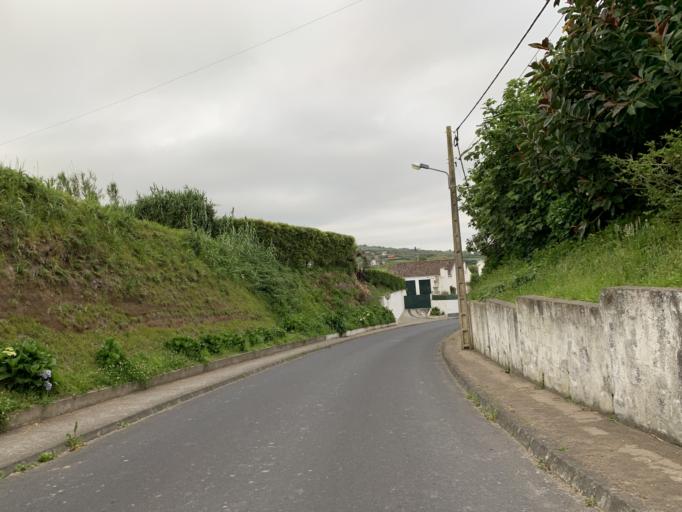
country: PT
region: Azores
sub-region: Ponta Delgada
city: Arrifes
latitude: 37.8480
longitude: -25.8407
